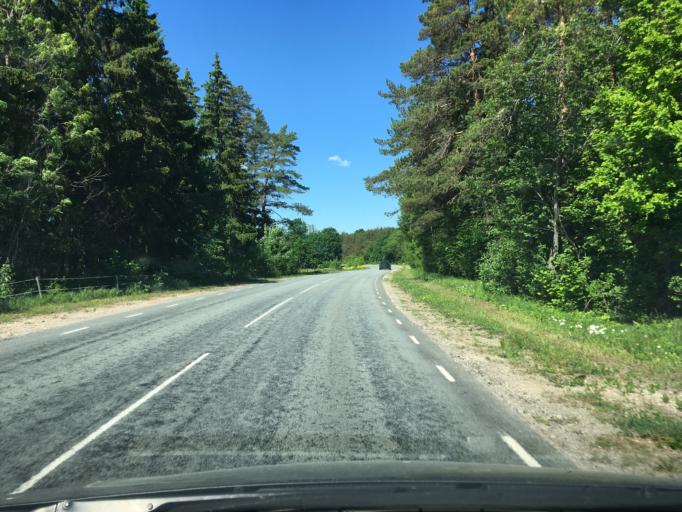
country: EE
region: Harju
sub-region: Rae vald
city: Vaida
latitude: 59.2016
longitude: 24.9566
